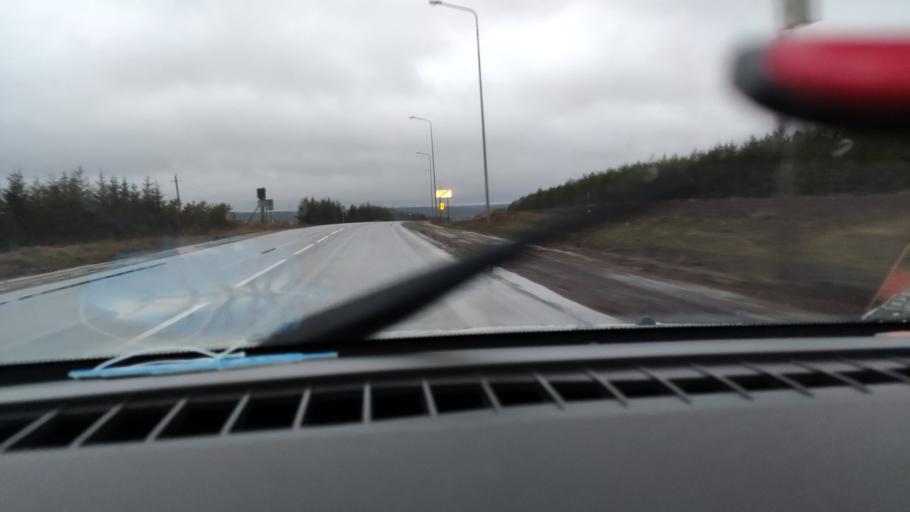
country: RU
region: Udmurtiya
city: Alnashi
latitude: 56.1694
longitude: 52.4767
